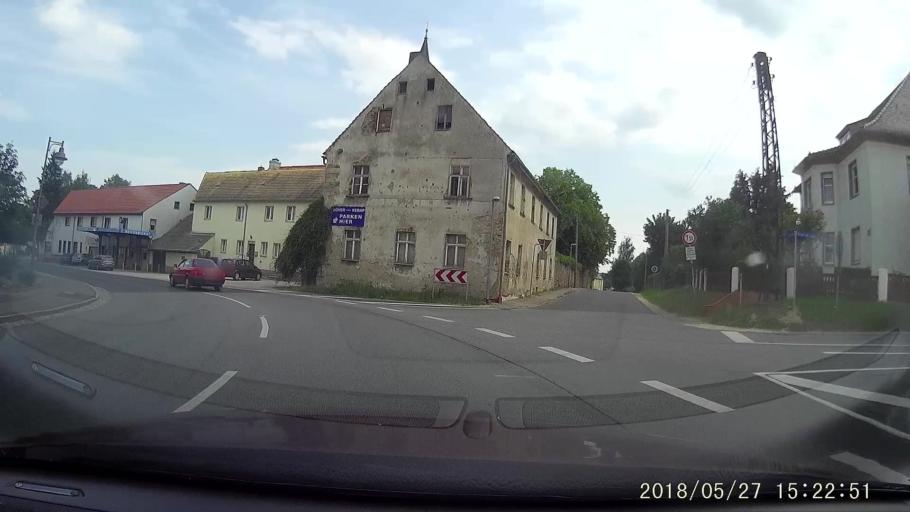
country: DE
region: Saxony
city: Kodersdorf
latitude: 51.2306
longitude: 14.8924
